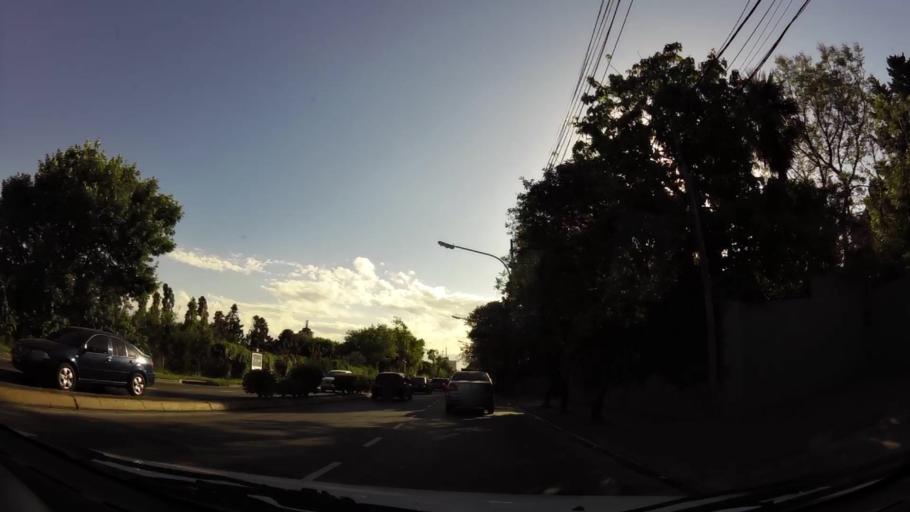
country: AR
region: Buenos Aires
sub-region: Partido de San Isidro
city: San Isidro
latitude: -34.4901
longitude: -58.5432
